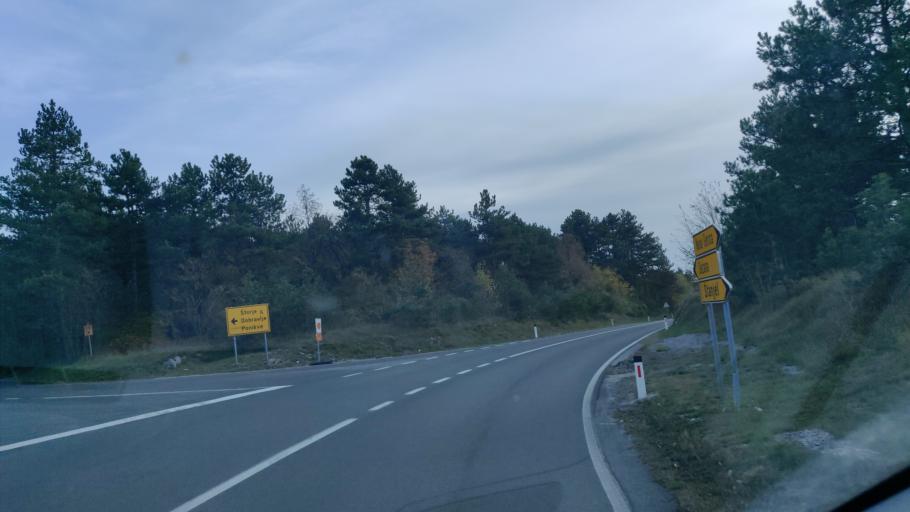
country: IT
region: Friuli Venezia Giulia
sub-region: Provincia di Trieste
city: Zolla
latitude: 45.8054
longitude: 13.8452
